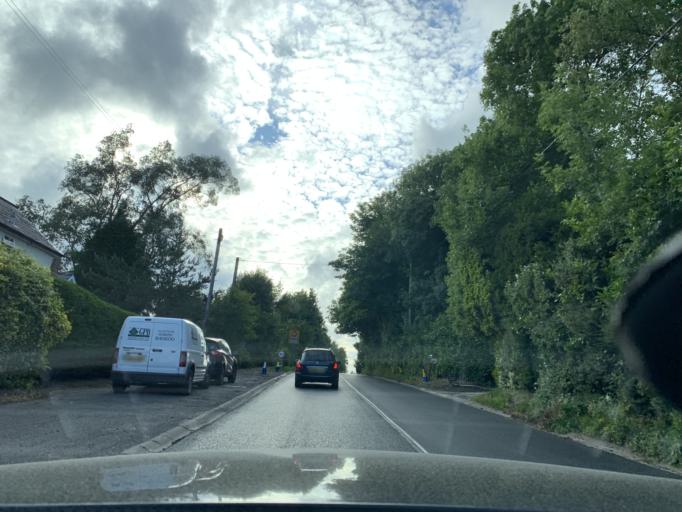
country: GB
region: England
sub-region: East Sussex
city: Robertsbridge
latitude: 50.9568
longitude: 0.4967
